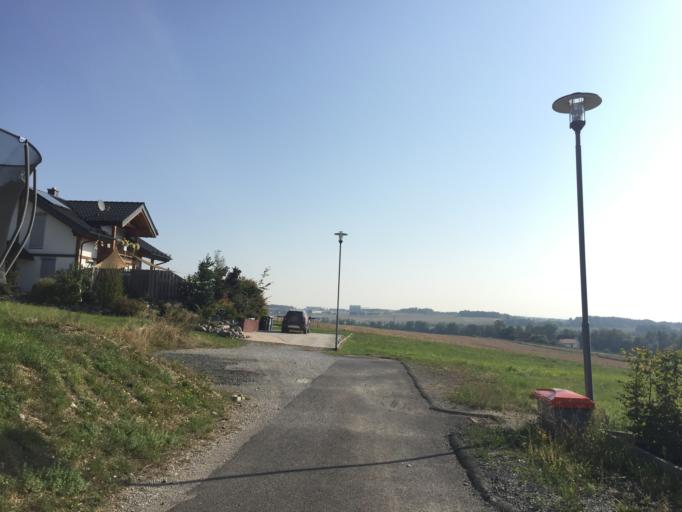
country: DE
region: Hesse
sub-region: Regierungsbezirk Giessen
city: Hoernsheim
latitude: 50.4640
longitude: 8.6009
